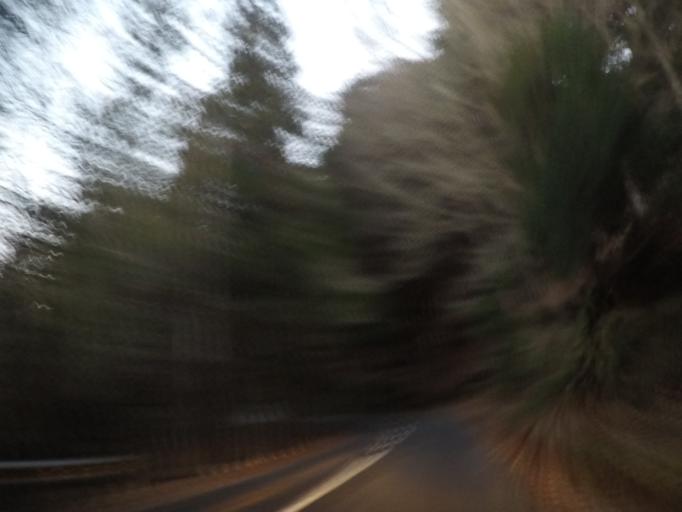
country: PT
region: Madeira
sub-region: Santa Cruz
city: Camacha
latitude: 32.7186
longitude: -16.8538
